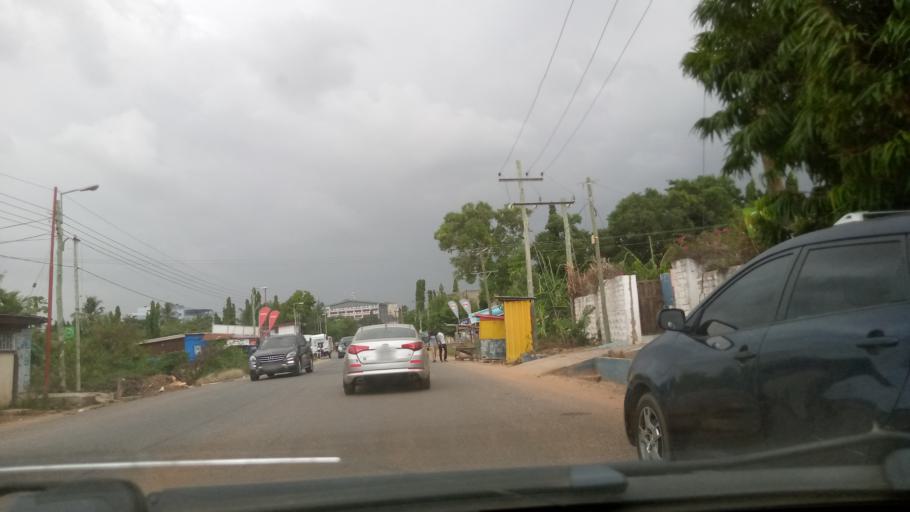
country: GH
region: Greater Accra
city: Accra
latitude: 5.6139
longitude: -0.1903
